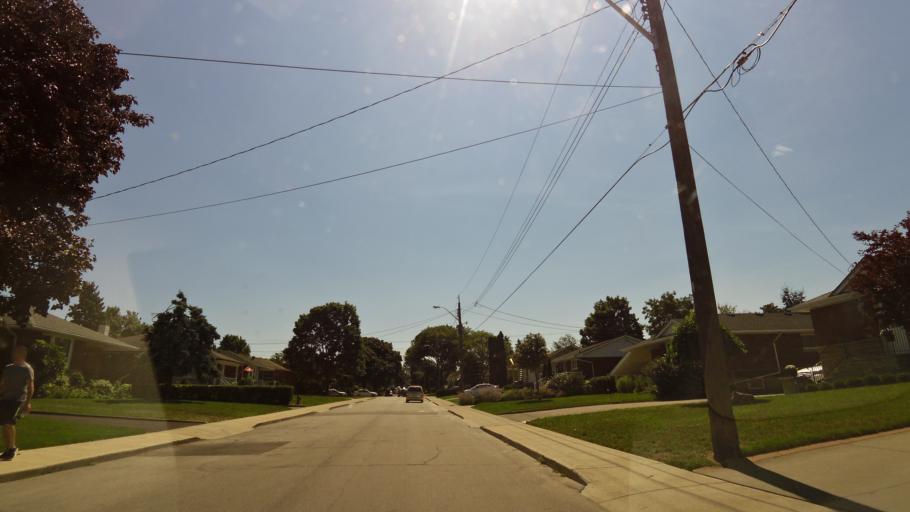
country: CA
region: Ontario
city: Hamilton
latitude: 43.2382
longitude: -79.9023
